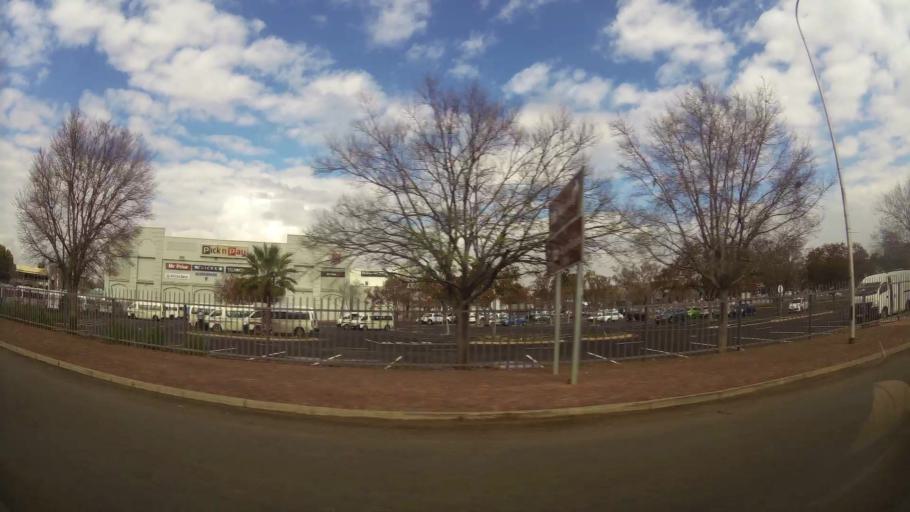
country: ZA
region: Gauteng
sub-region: Sedibeng District Municipality
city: Vereeniging
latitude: -26.6597
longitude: 27.9707
